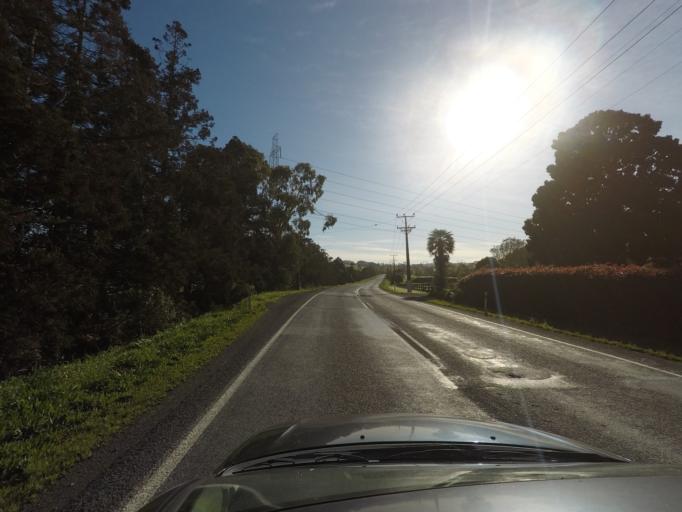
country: NZ
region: Auckland
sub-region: Auckland
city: Red Hill
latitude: -37.0016
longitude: 174.9602
